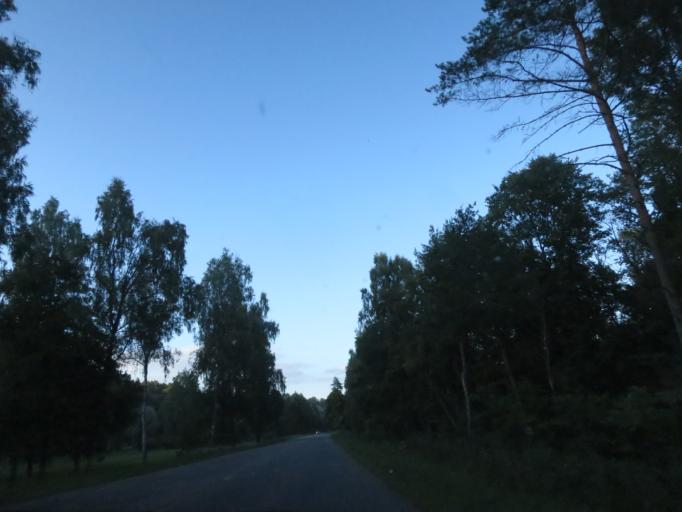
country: LV
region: Sigulda
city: Sigulda
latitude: 57.1732
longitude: 24.8415
